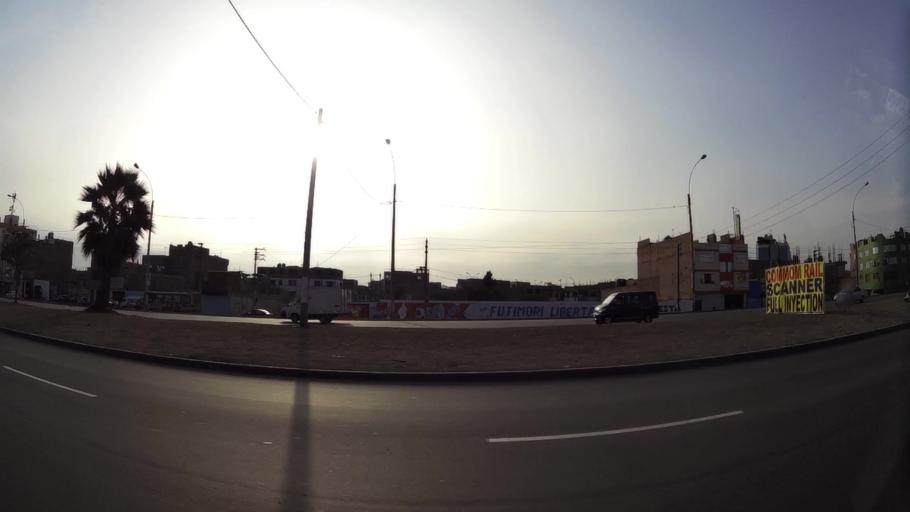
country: PE
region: Lima
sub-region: Lima
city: Independencia
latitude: -11.9827
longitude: -77.0979
